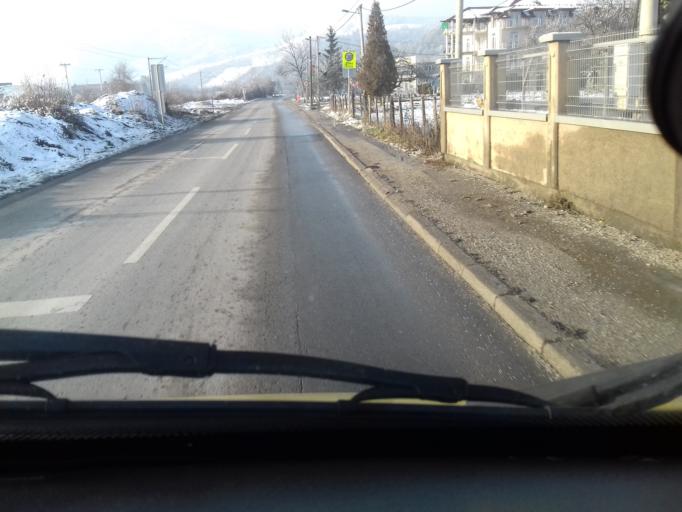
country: BA
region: Federation of Bosnia and Herzegovina
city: Mahala
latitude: 43.9926
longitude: 18.2250
